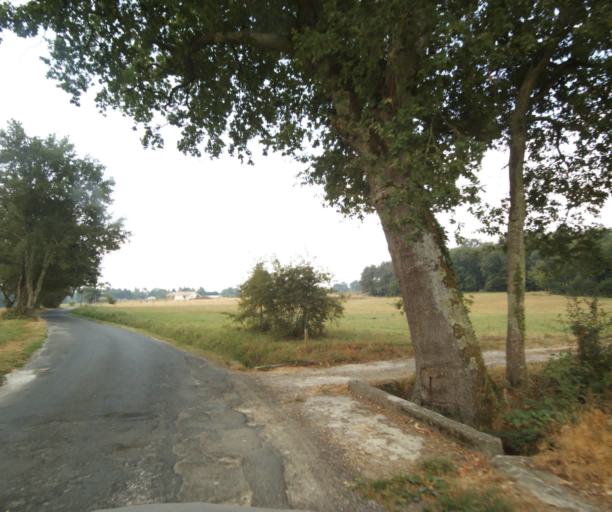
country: FR
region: Aquitaine
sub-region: Departement de la Gironde
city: La Sauve
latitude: 44.7803
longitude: -0.3215
